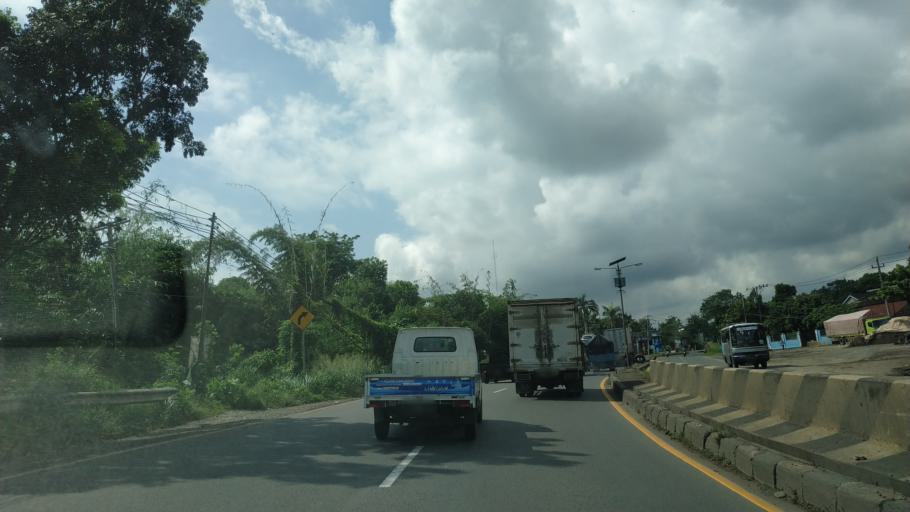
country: ID
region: Central Java
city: Pekalongan
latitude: -6.9245
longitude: 109.7620
